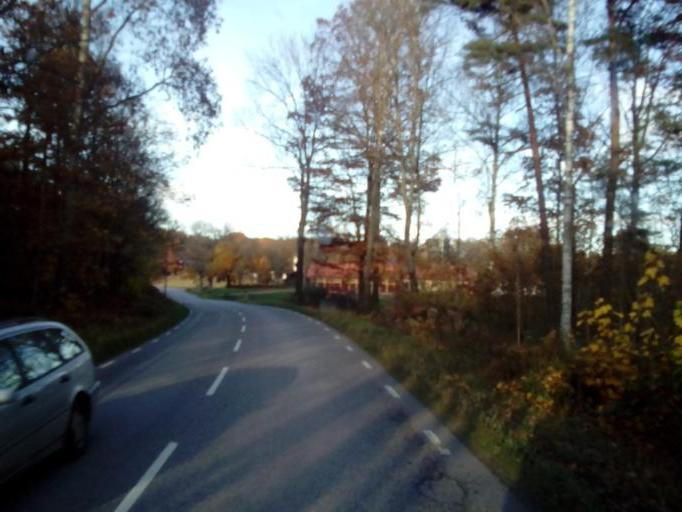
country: SE
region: Kalmar
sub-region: Vimmerby Kommun
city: Vimmerby
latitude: 57.7209
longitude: 16.0687
